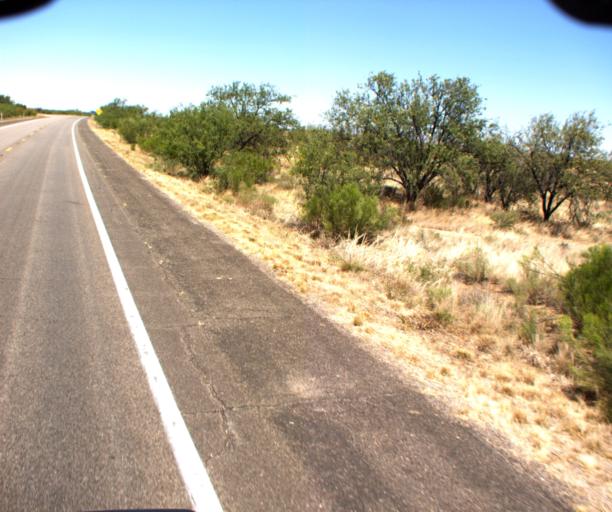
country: US
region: Arizona
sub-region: Pima County
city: Catalina
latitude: 32.5681
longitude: -110.9434
